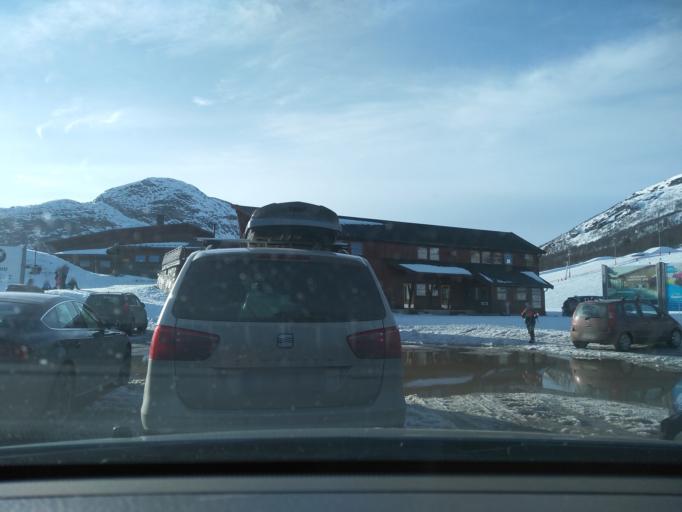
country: NO
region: Aust-Agder
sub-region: Bykle
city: Hovden
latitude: 59.5691
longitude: 7.3503
